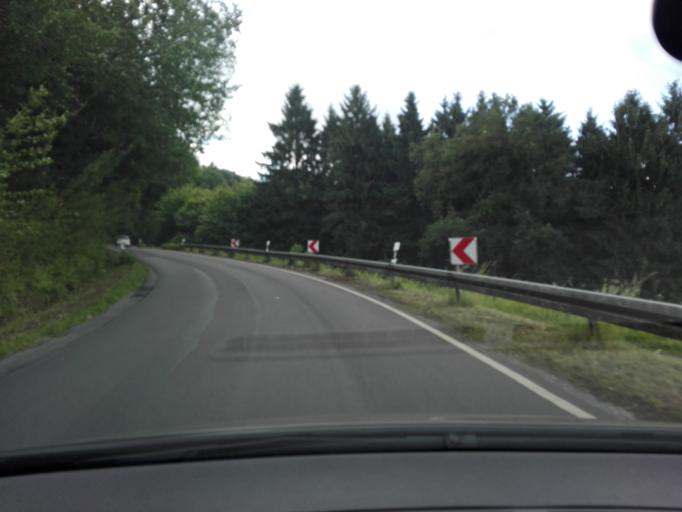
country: DE
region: North Rhine-Westphalia
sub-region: Regierungsbezirk Arnsberg
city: Frondenberg
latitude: 51.4859
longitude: 7.7575
